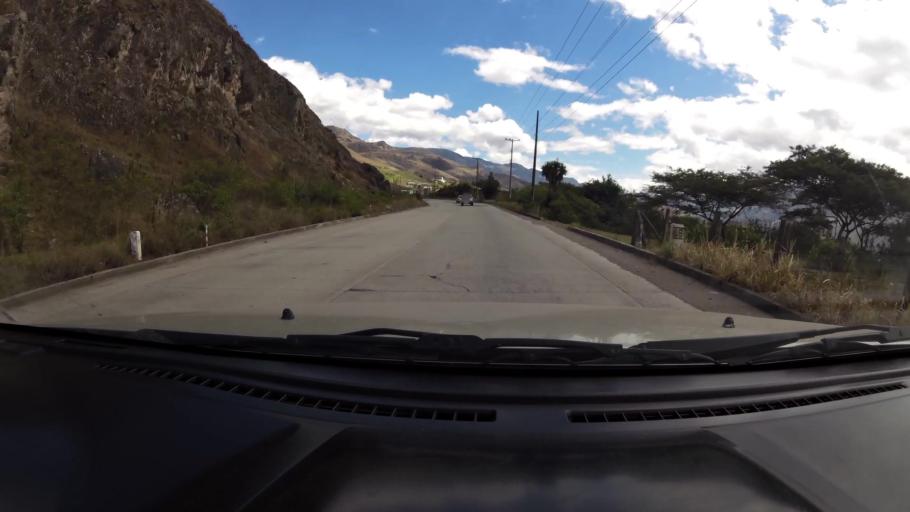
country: EC
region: Azuay
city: Cuenca
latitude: -3.2039
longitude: -79.1841
